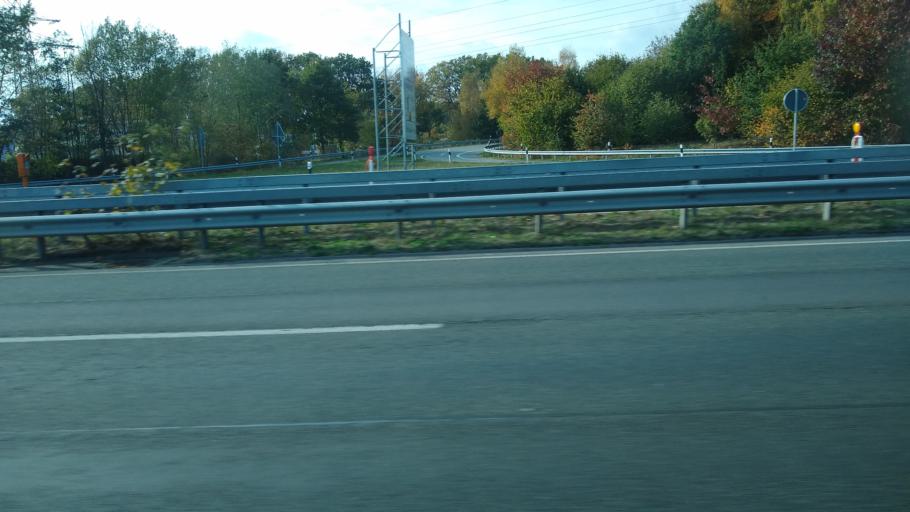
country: DE
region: Lower Saxony
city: Oldenburg
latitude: 53.1840
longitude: 8.2268
